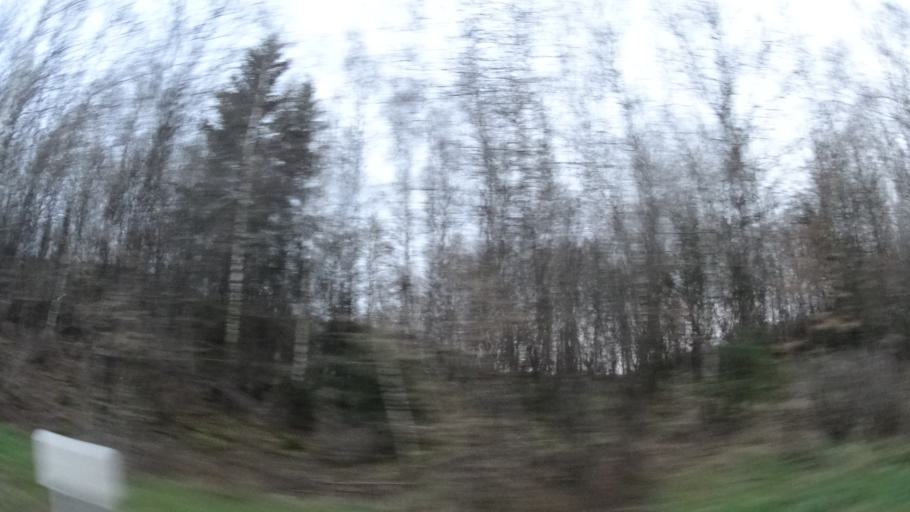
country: DE
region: Rheinland-Pfalz
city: Dambach
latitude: 49.6225
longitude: 7.1257
